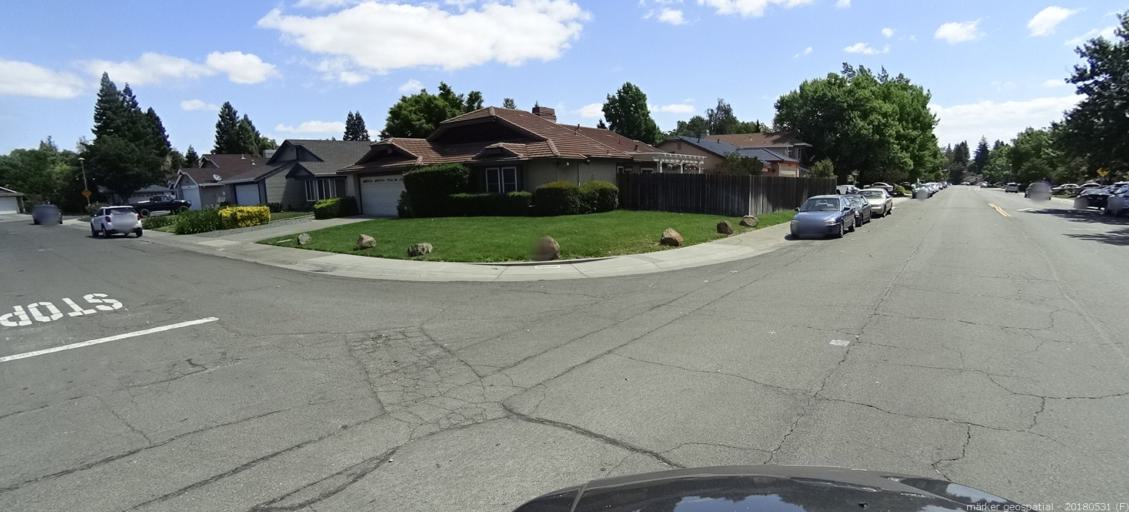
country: US
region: California
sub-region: Sacramento County
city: Sacramento
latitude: 38.6213
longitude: -121.5016
